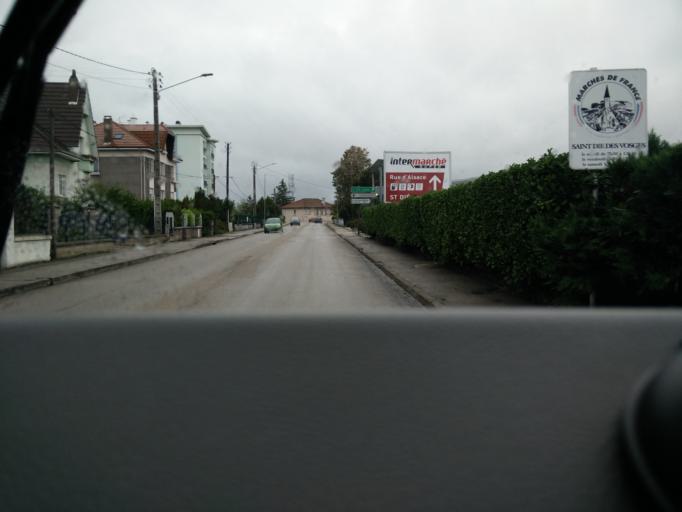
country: FR
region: Lorraine
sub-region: Departement des Vosges
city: Saint-Die-des-Vosges
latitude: 48.2744
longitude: 6.9613
